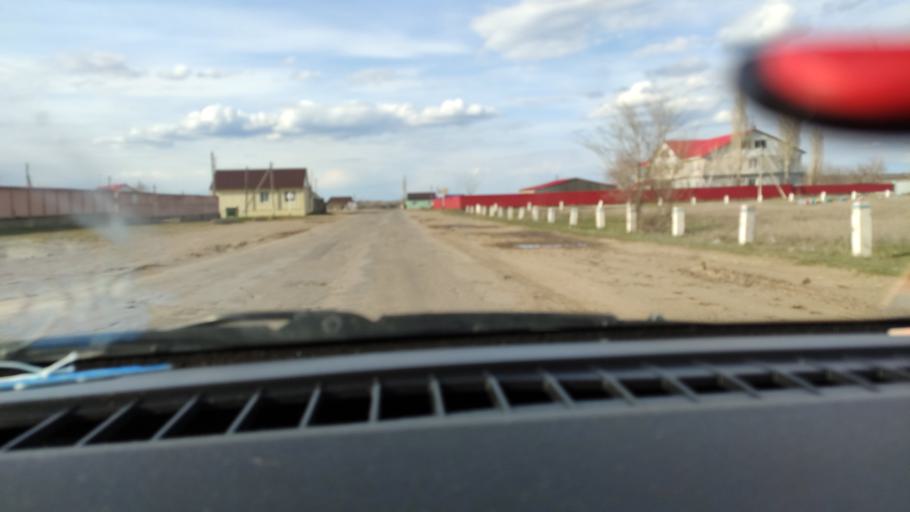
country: RU
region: Saratov
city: Rovnoye
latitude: 51.0278
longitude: 46.0909
